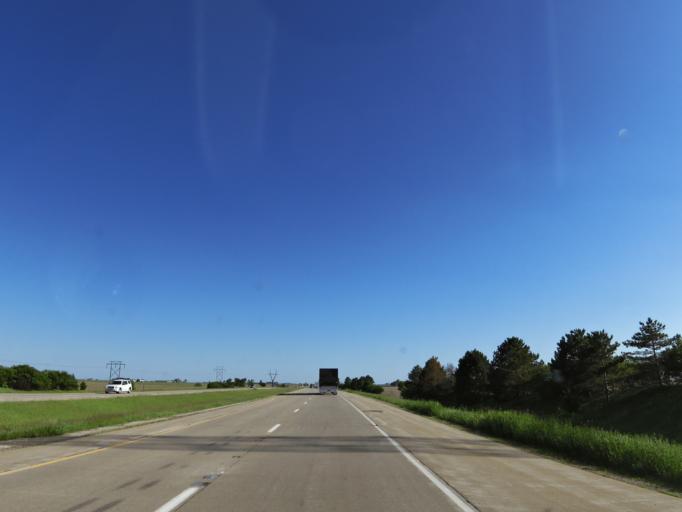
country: US
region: Illinois
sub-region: LaSalle County
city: Oglesby
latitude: 41.2065
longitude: -89.0780
